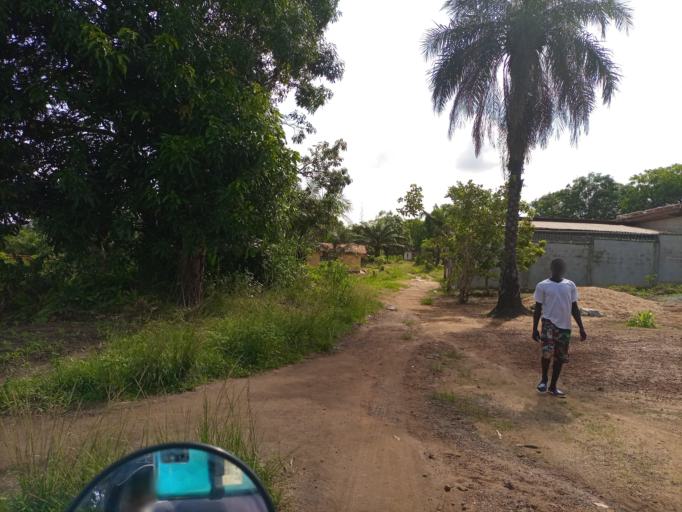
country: SL
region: Southern Province
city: Bo
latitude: 7.9660
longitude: -11.7655
